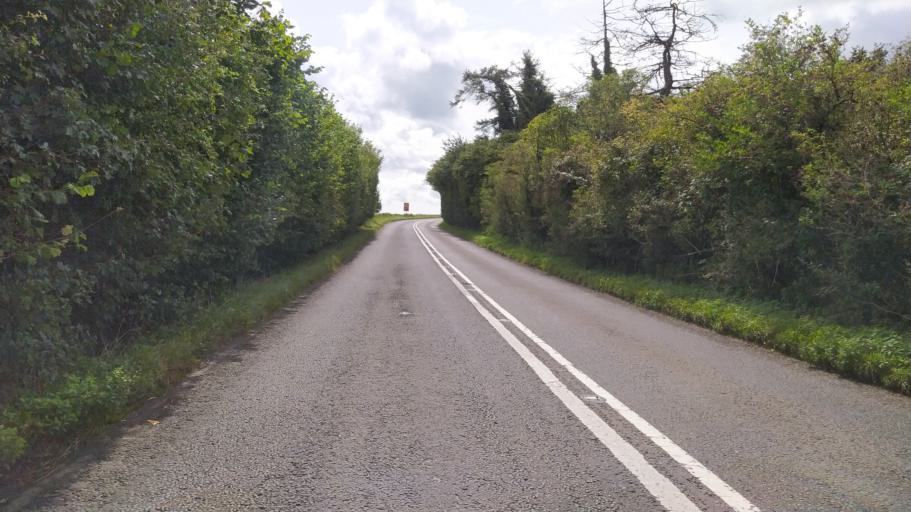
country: GB
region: England
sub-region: Wiltshire
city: Hindon
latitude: 51.0905
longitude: -2.1654
